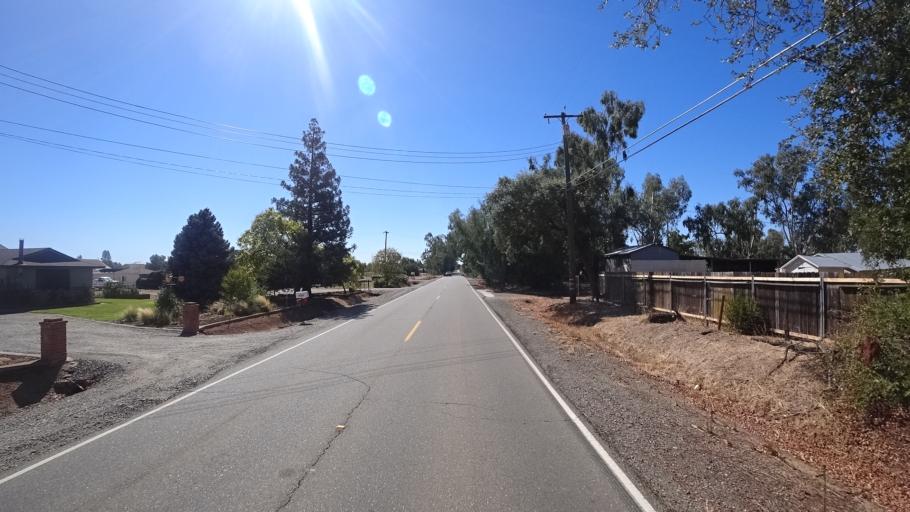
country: US
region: California
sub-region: Sacramento County
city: Vineyard
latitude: 38.4467
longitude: -121.3254
